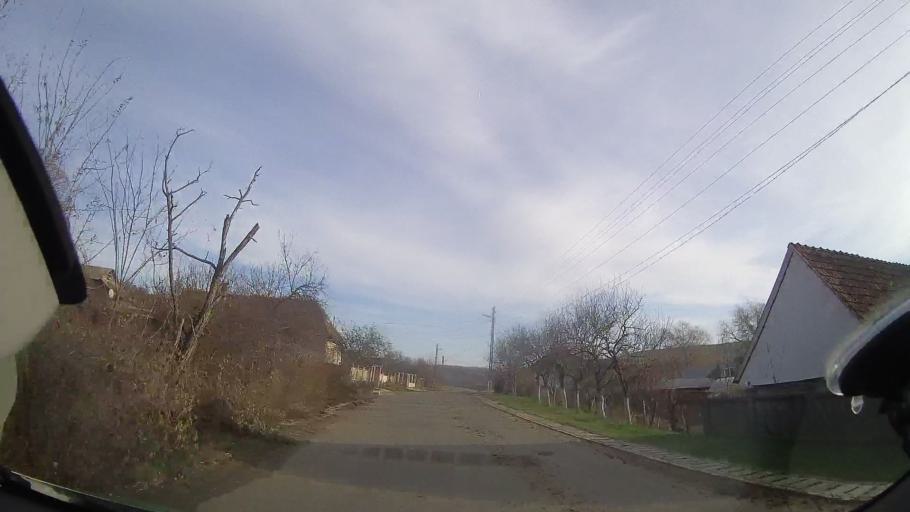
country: RO
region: Bihor
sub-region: Comuna Sarbi
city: Burzuc
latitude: 47.1475
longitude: 22.1795
